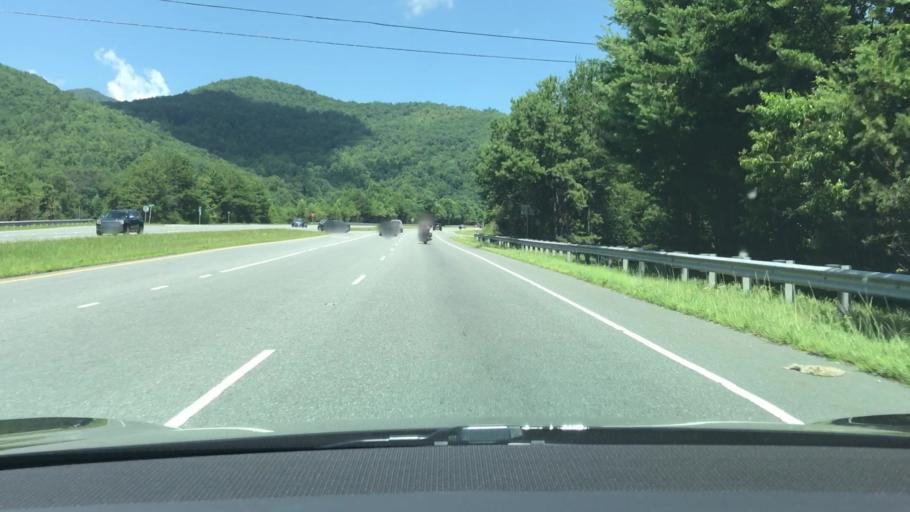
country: US
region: North Carolina
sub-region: Jackson County
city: Sylva
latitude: 35.3409
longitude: -83.2536
